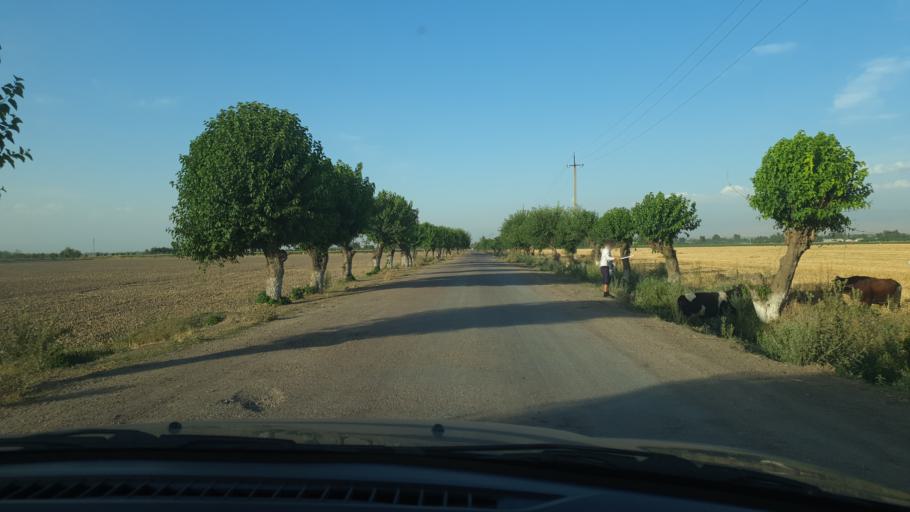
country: UZ
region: Toshkent
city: Tuytepa
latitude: 41.0983
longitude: 69.3774
